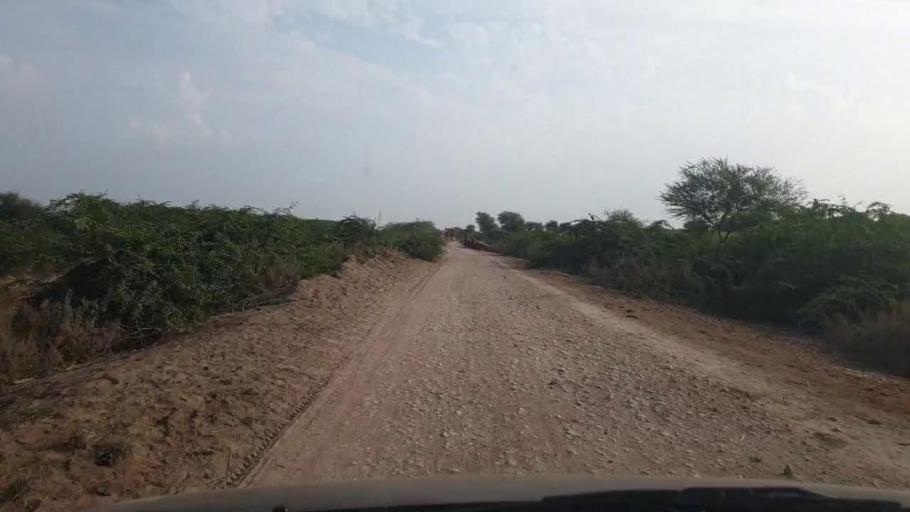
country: PK
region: Sindh
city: Badin
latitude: 24.5672
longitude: 68.6671
